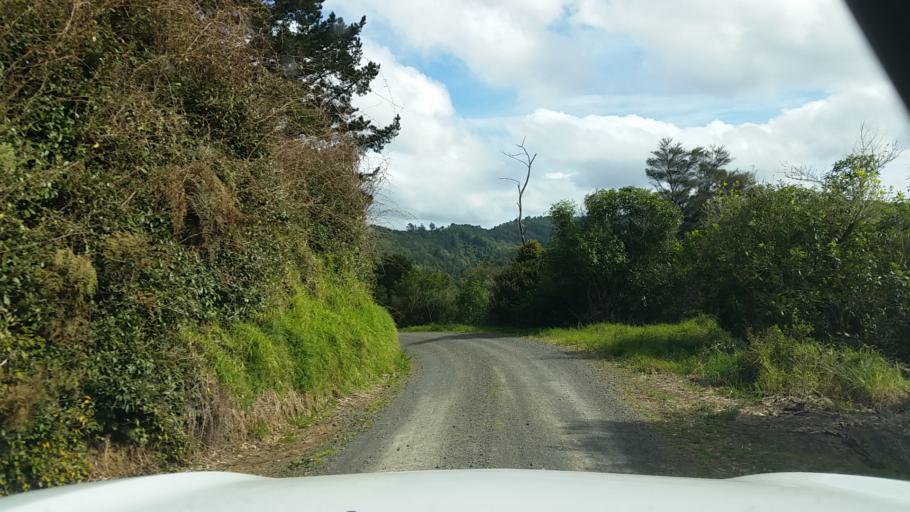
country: NZ
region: Waikato
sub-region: Hauraki District
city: Ngatea
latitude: -37.4638
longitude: 175.4652
